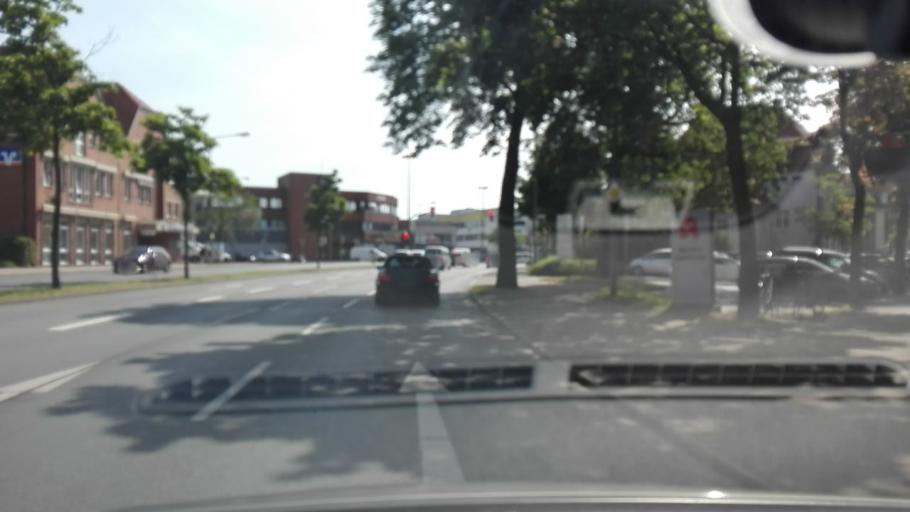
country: DE
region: North Rhine-Westphalia
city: Lunen
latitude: 51.6186
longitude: 7.5228
